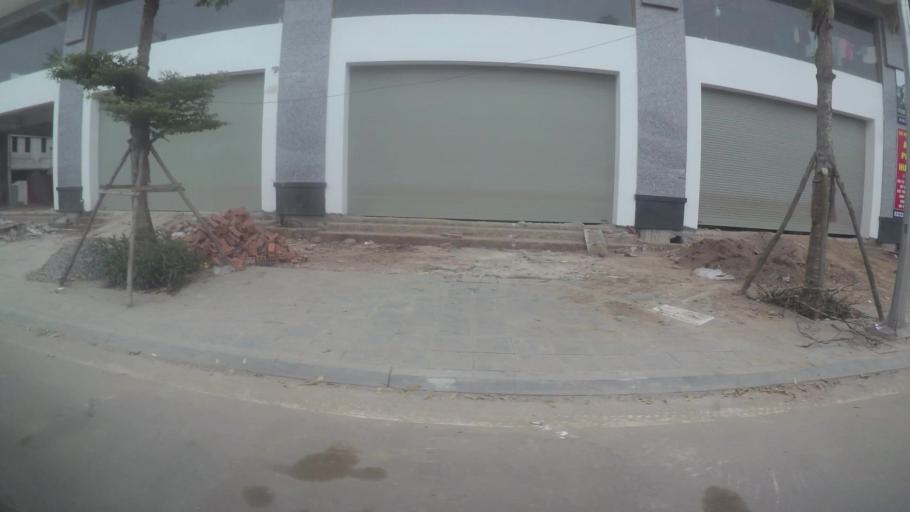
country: VN
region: Ha Noi
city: Ha Dong
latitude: 20.9857
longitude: 105.7398
